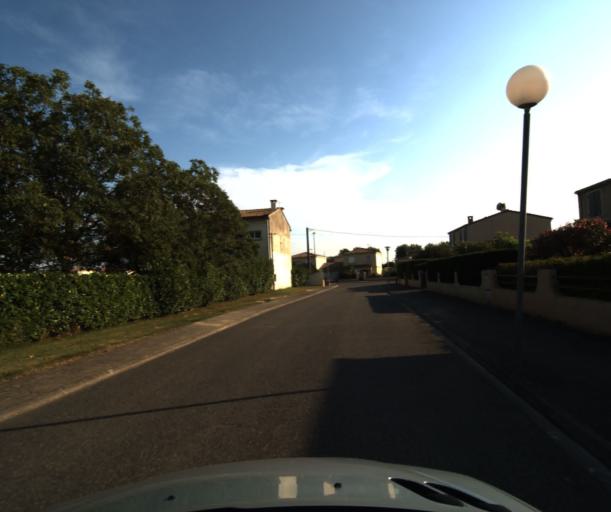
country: FR
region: Midi-Pyrenees
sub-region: Departement de la Haute-Garonne
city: Roquettes
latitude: 43.4802
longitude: 1.3881
